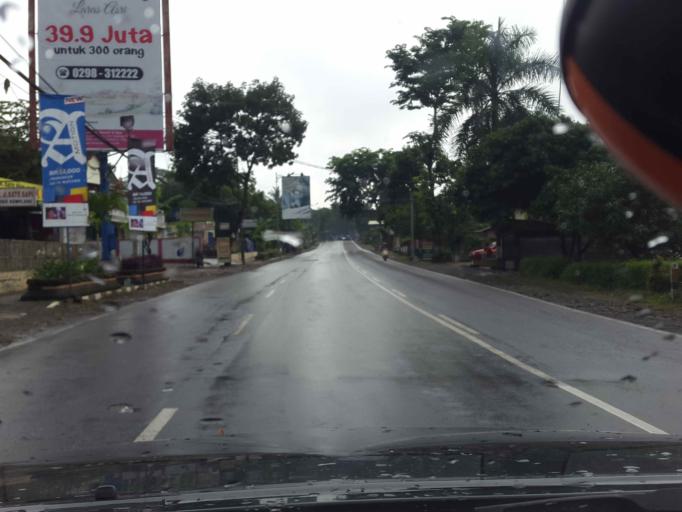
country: ID
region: Central Java
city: Salatiga
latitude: -7.2943
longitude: 110.4751
